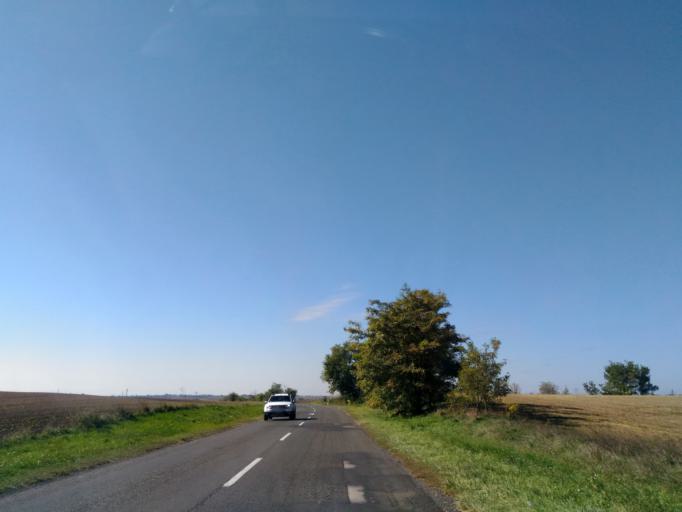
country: HU
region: Fejer
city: Ivancsa
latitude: 47.1746
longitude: 18.7973
